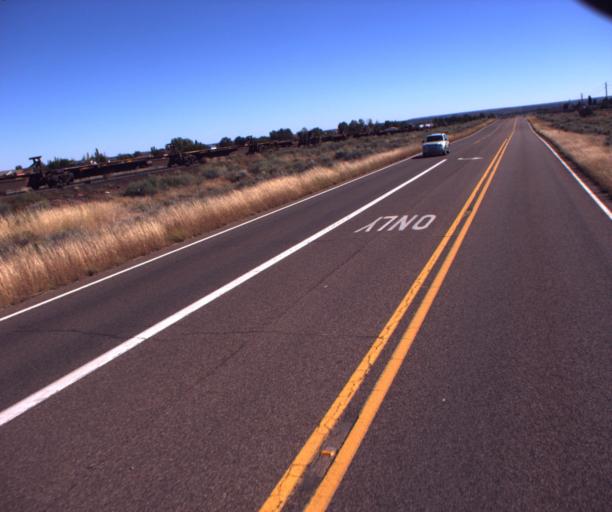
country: US
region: Arizona
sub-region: Navajo County
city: Snowflake
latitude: 34.5130
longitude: -110.1266
